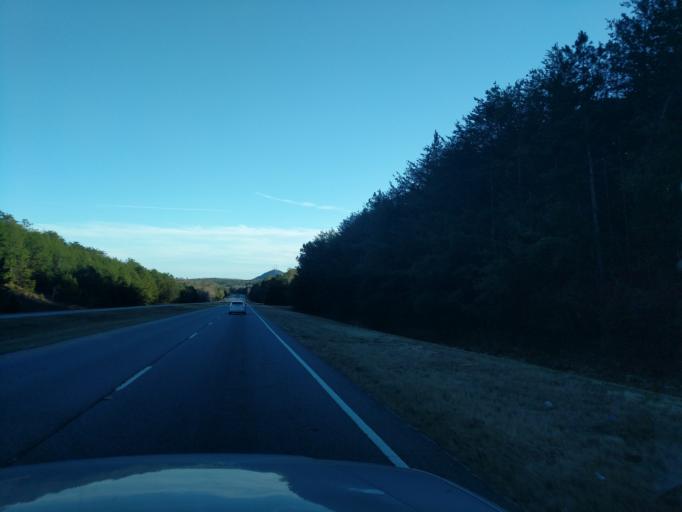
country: US
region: Georgia
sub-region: Stephens County
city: Toccoa
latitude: 34.5776
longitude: -83.4067
